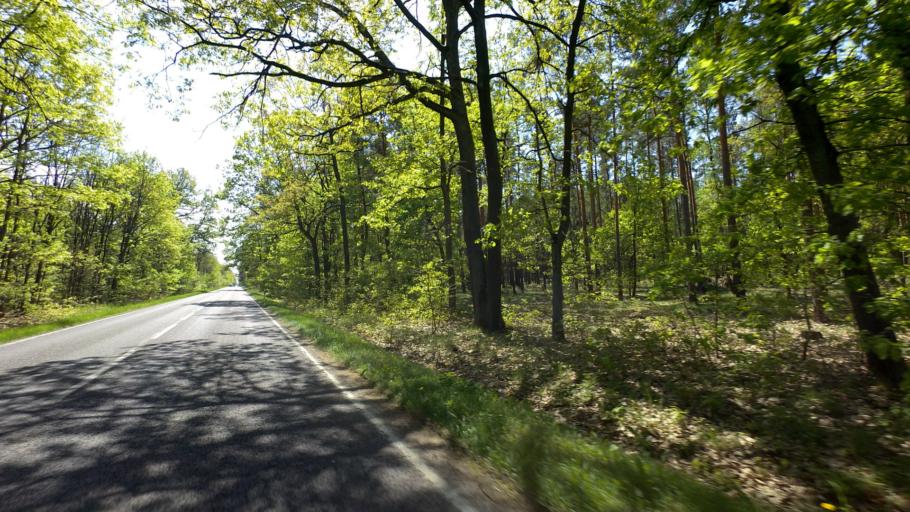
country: DE
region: Brandenburg
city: Bestensee
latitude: 52.2180
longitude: 13.6861
